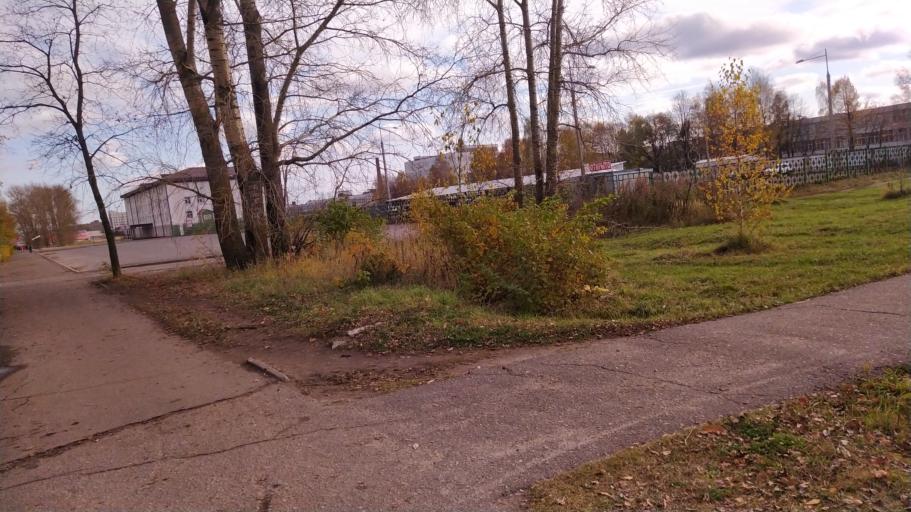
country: RU
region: Jaroslavl
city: Rybinsk
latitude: 58.0561
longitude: 38.8003
